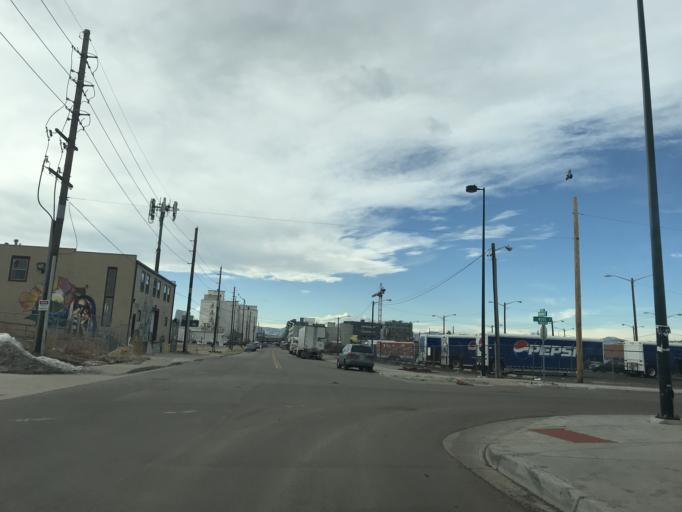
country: US
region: Colorado
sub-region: Denver County
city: Denver
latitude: 39.7741
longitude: -104.9722
